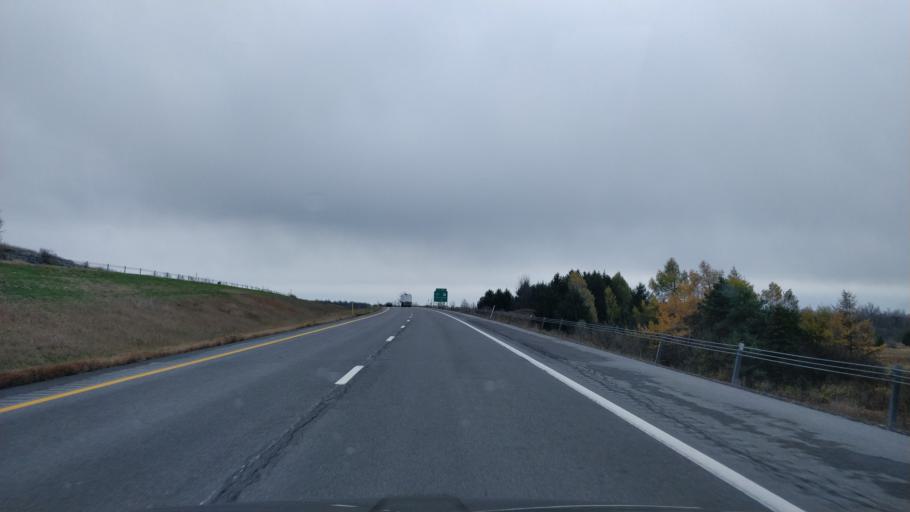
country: US
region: New York
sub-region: Jefferson County
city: Brownville
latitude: 44.0609
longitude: -75.9211
